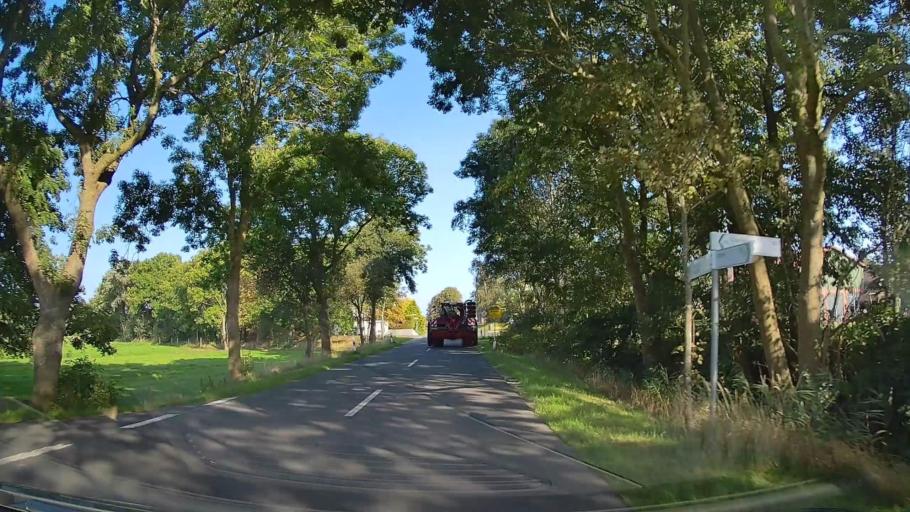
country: DE
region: Lower Saxony
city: Nordholz
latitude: 53.7736
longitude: 8.5835
